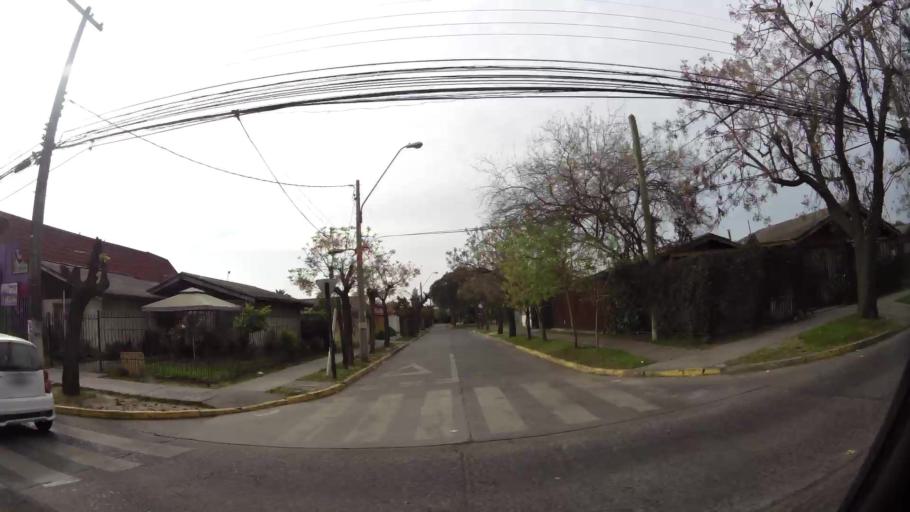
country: CL
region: Santiago Metropolitan
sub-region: Provincia de Santiago
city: Lo Prado
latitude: -33.5212
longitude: -70.7644
